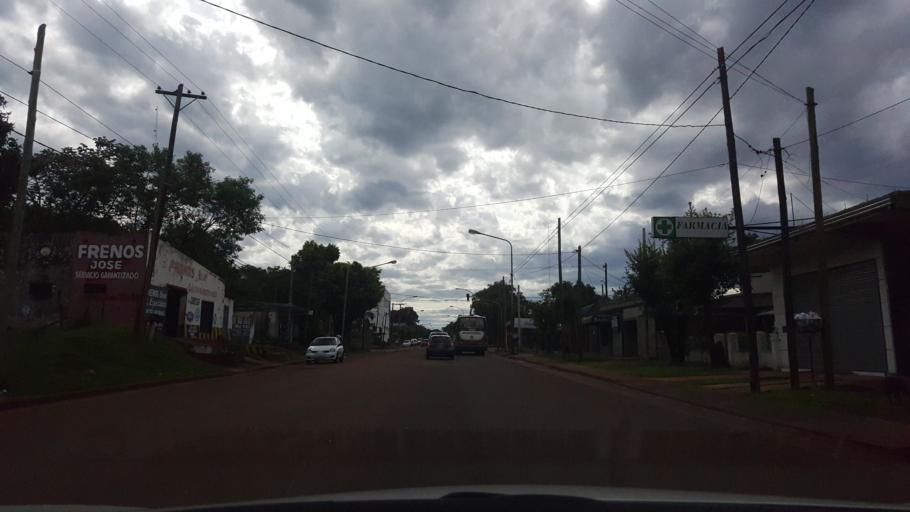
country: AR
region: Misiones
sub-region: Departamento de Capital
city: Posadas
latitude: -27.3699
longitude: -55.9387
